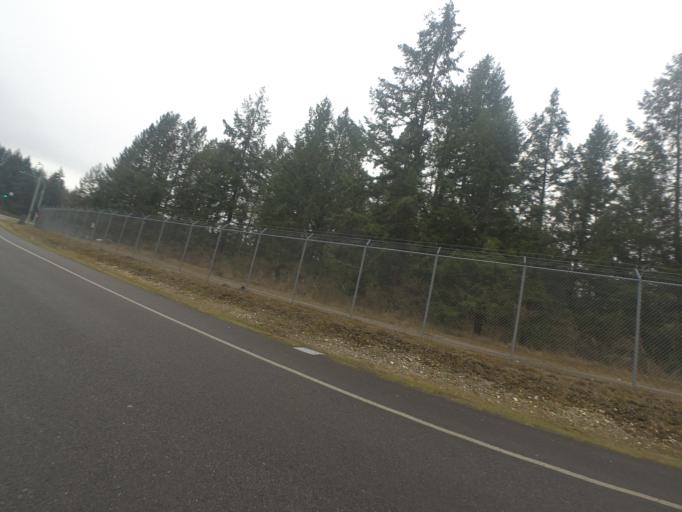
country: US
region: Washington
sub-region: Pierce County
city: McChord Air Force Base
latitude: 47.1144
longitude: -122.4929
